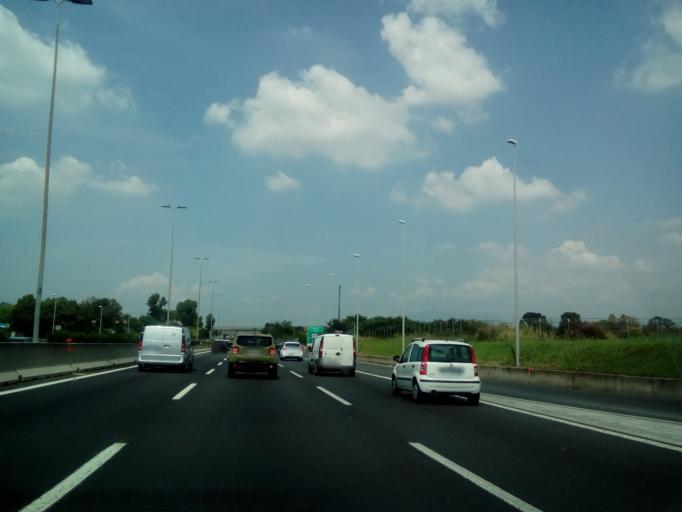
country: IT
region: Latium
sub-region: Citta metropolitana di Roma Capitale
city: Ciampino
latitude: 41.8758
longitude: 12.6075
